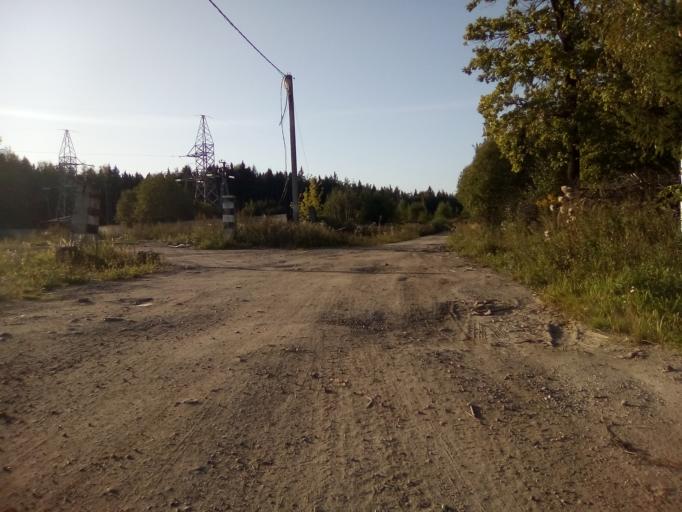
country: RU
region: Moskovskaya
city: Aprelevka
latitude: 55.5682
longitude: 37.0672
